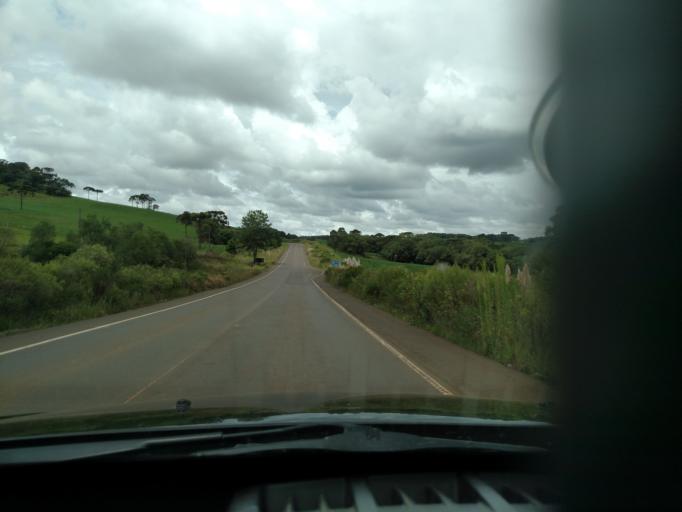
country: BR
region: Rio Grande do Sul
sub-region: Vacaria
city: Estrela
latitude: -27.9186
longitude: -50.6625
